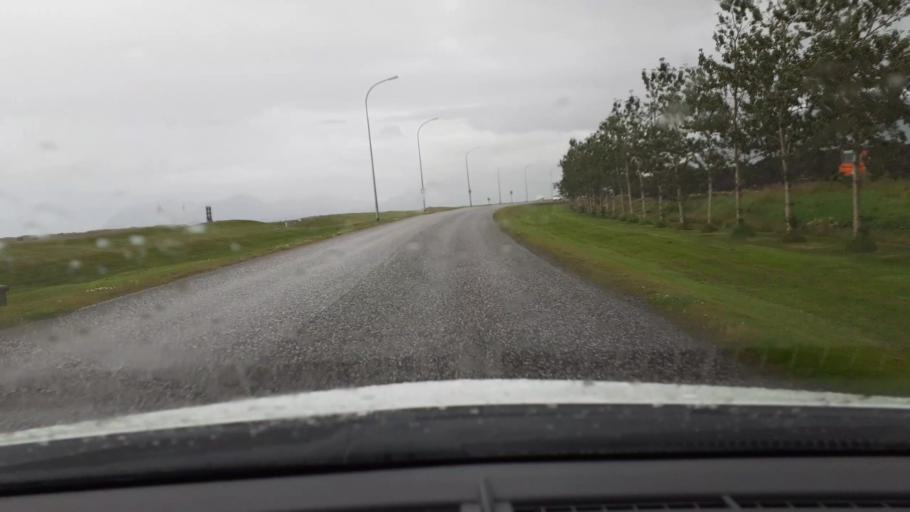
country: IS
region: West
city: Akranes
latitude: 64.3255
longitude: -22.0669
